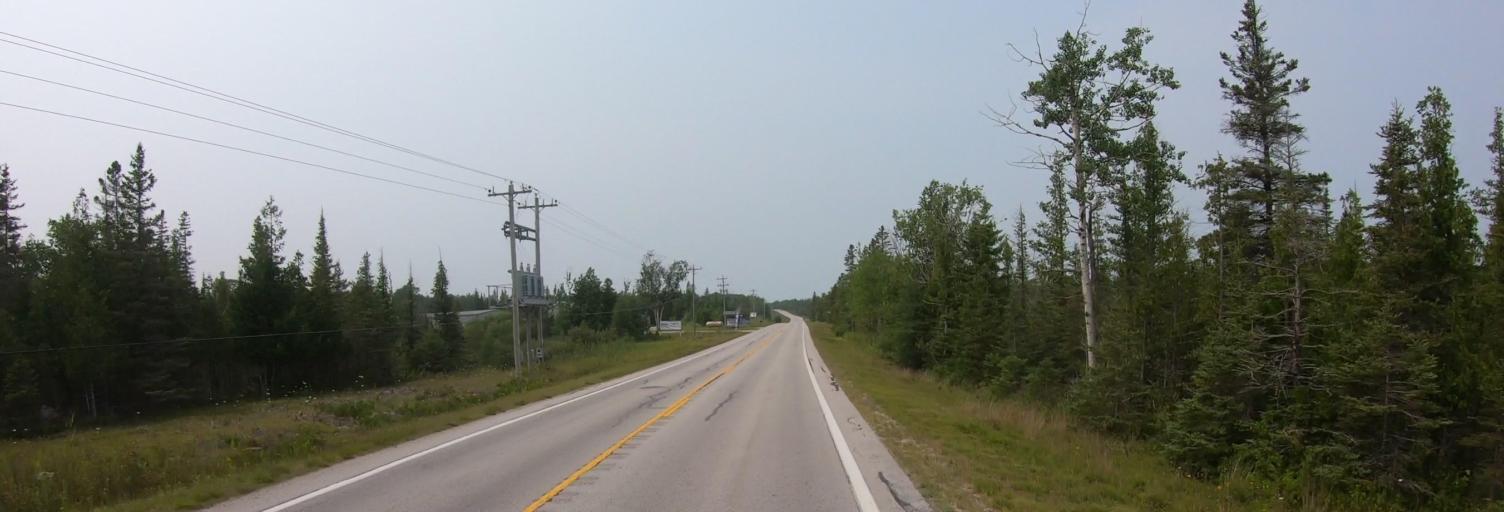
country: CA
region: Ontario
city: Thessalon
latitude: 45.9852
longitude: -83.8119
